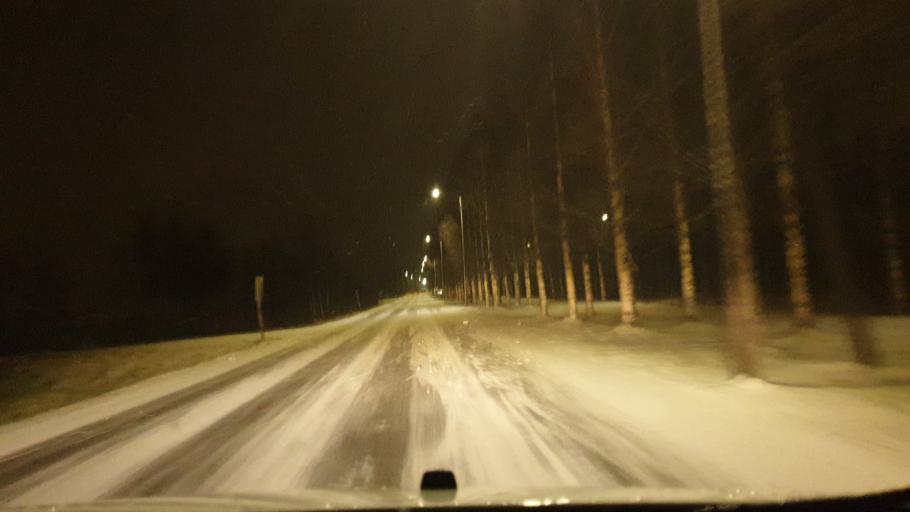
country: FI
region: Northern Ostrobothnia
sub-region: Oulu
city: Oulu
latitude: 64.9918
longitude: 25.4427
